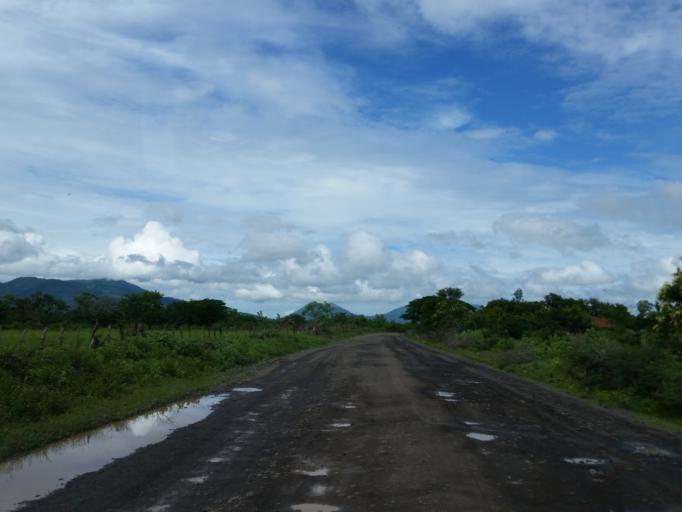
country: NI
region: Leon
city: Larreynaga
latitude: 12.5889
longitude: -86.6548
